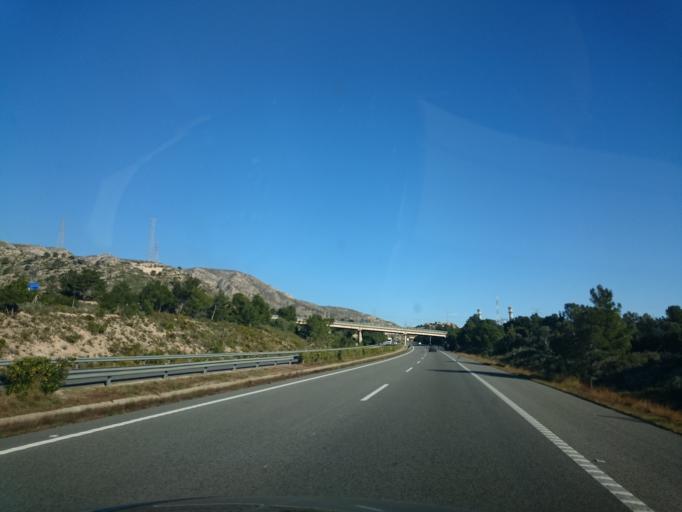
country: ES
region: Catalonia
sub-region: Provincia de Tarragona
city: l'Ametlla de Mar
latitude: 40.9508
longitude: 0.8613
